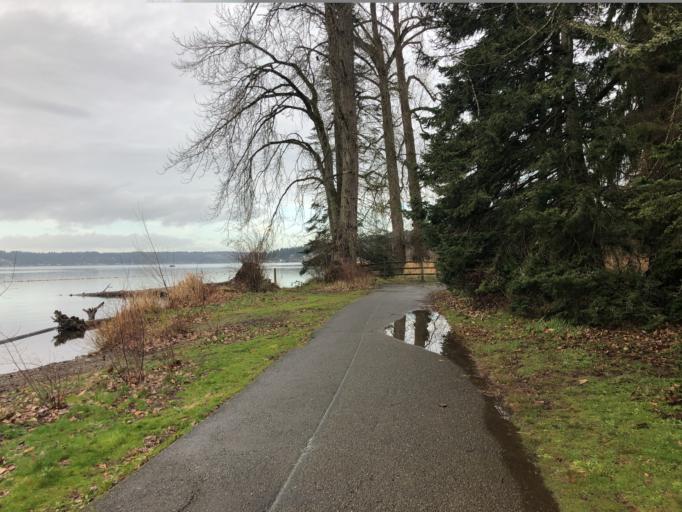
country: US
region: Washington
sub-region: King County
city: West Lake Sammamish
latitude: 47.5600
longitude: -122.0647
